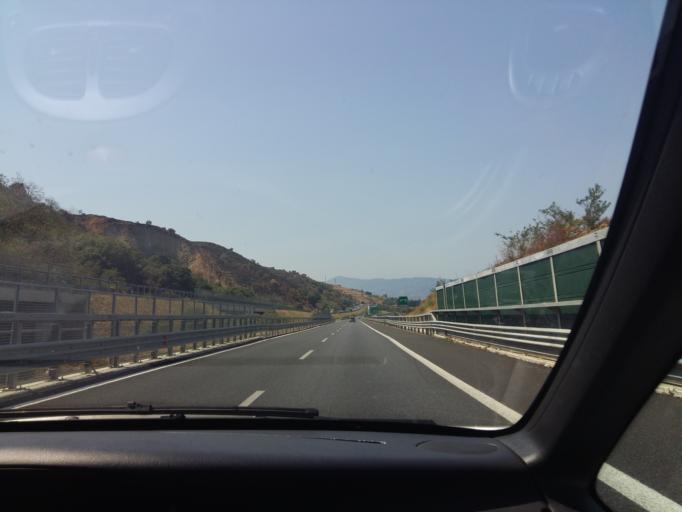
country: IT
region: Calabria
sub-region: Provincia di Reggio Calabria
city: Villa San Giovanni
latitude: 38.2331
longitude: 15.6684
